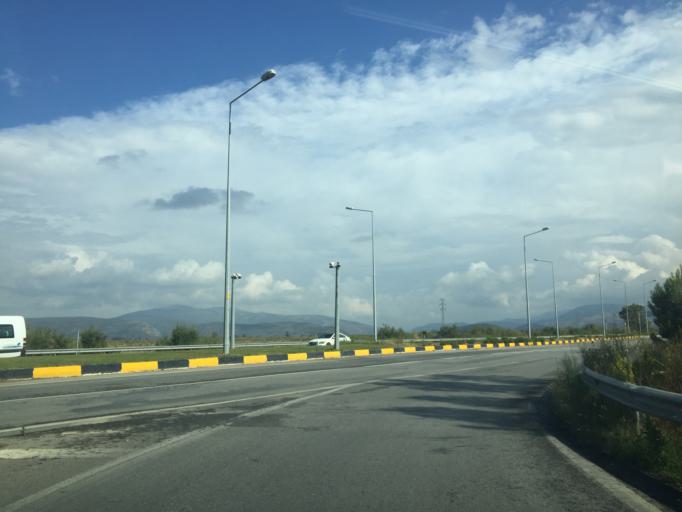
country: TR
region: Izmir
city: Selcuk
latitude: 37.9519
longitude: 27.2996
